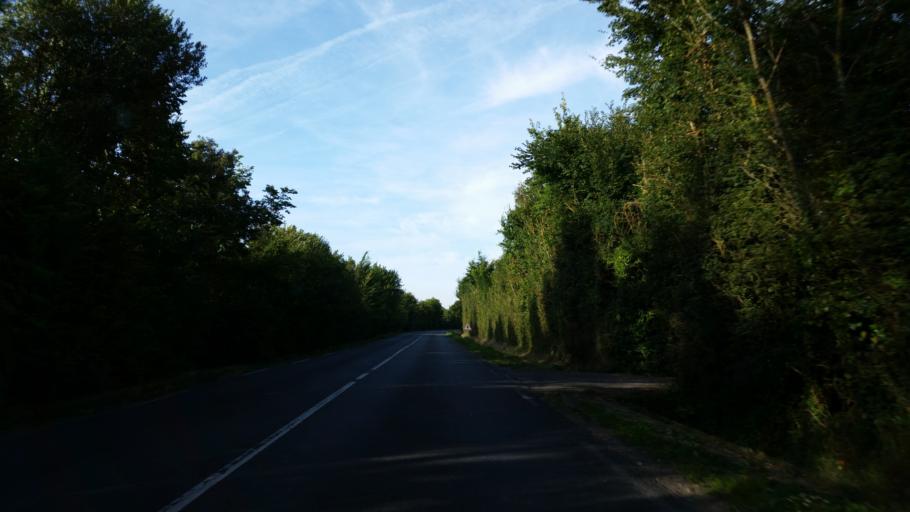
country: FR
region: Lower Normandy
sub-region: Departement du Calvados
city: Cambremer
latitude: 49.1695
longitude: 0.0057
